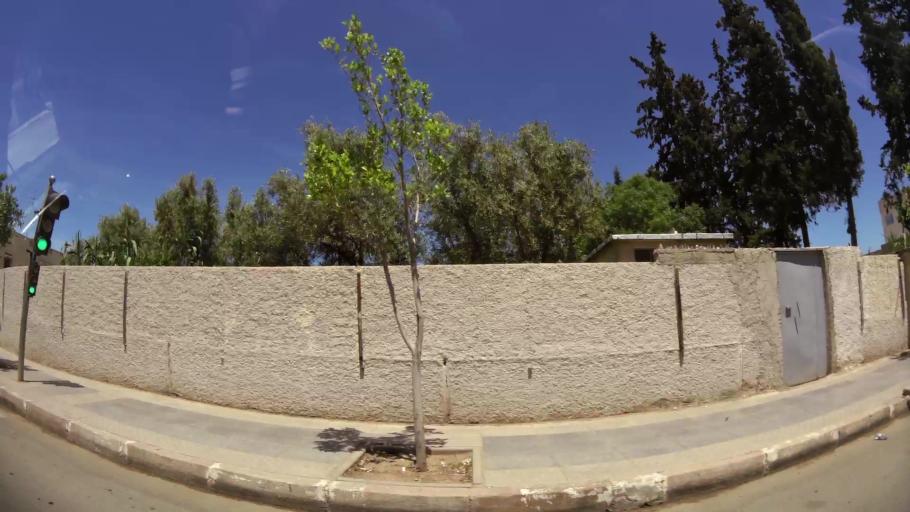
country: MA
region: Oriental
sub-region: Oujda-Angad
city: Oujda
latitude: 34.6736
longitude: -1.9172
